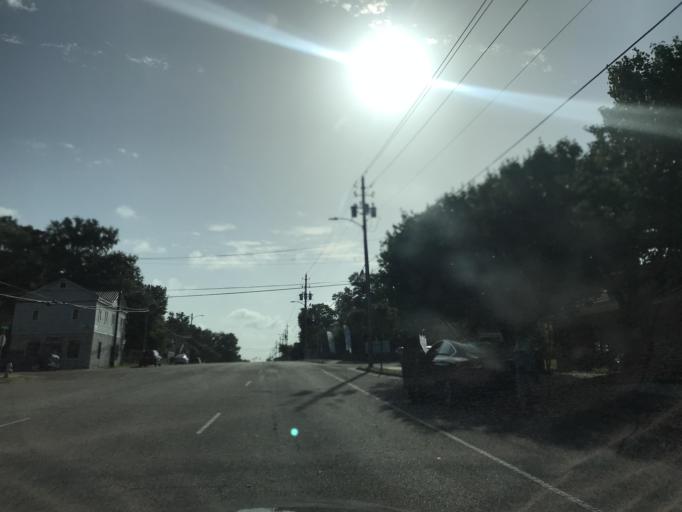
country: US
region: North Carolina
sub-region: New Hanover County
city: Wilmington
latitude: 34.2245
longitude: -77.9412
